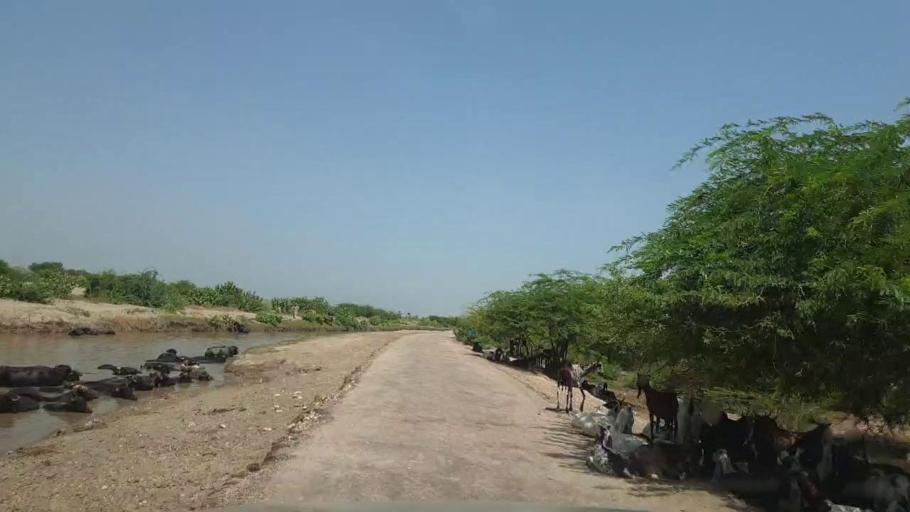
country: PK
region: Sindh
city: Rohri
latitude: 27.6219
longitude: 69.0980
